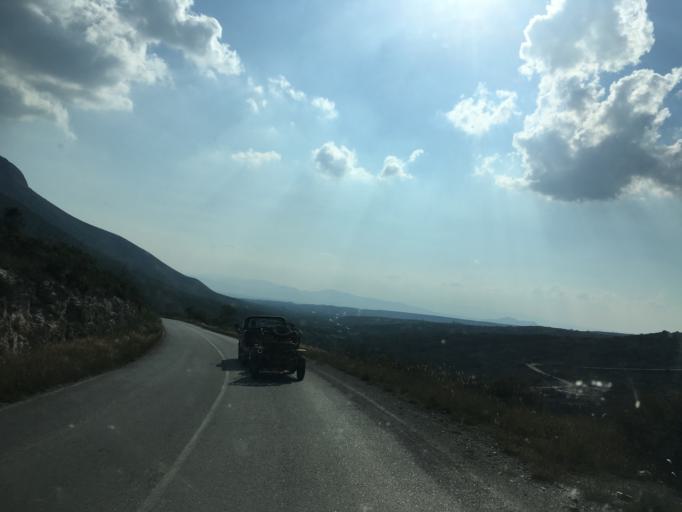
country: MX
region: Hidalgo
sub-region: Cardonal
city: Pozuelos
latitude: 20.6098
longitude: -99.1043
